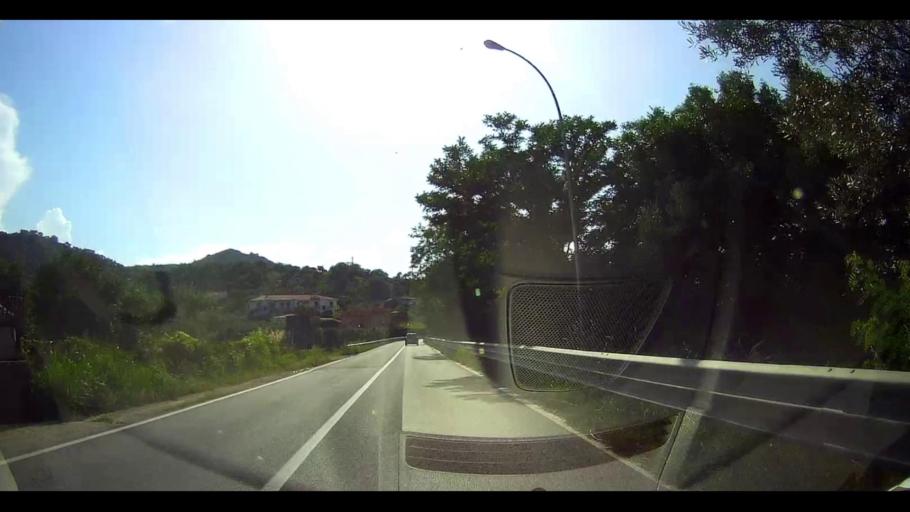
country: IT
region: Calabria
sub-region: Provincia di Cosenza
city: Cariati
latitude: 39.4843
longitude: 16.9715
